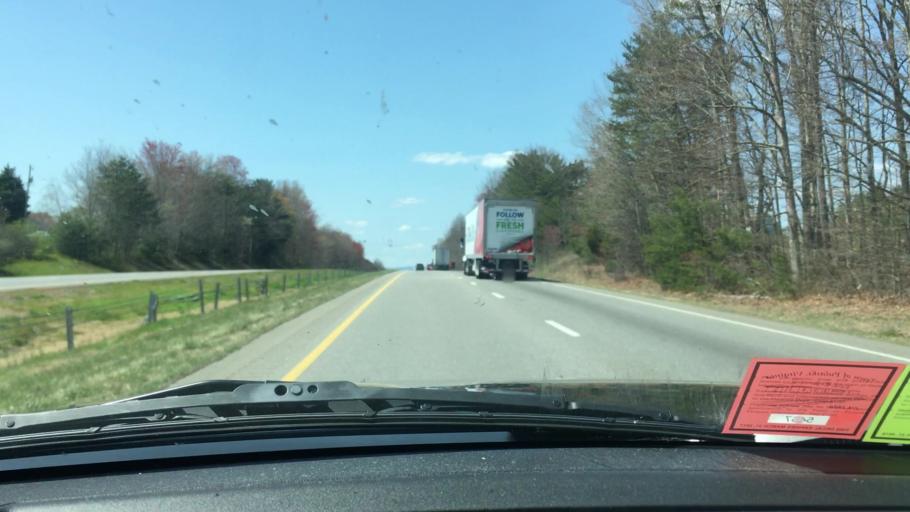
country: US
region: North Carolina
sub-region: Surry County
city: Pilot Mountain
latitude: 36.4173
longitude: -80.5100
